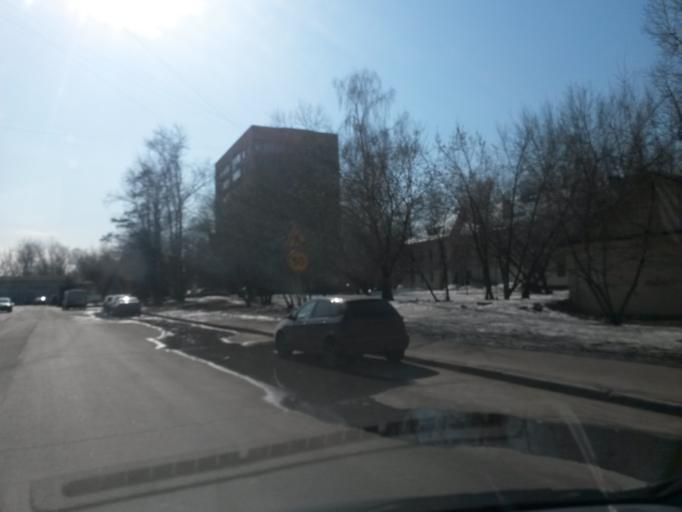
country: RU
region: Moskovskaya
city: Shcherbinka
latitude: 55.5405
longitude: 37.5731
